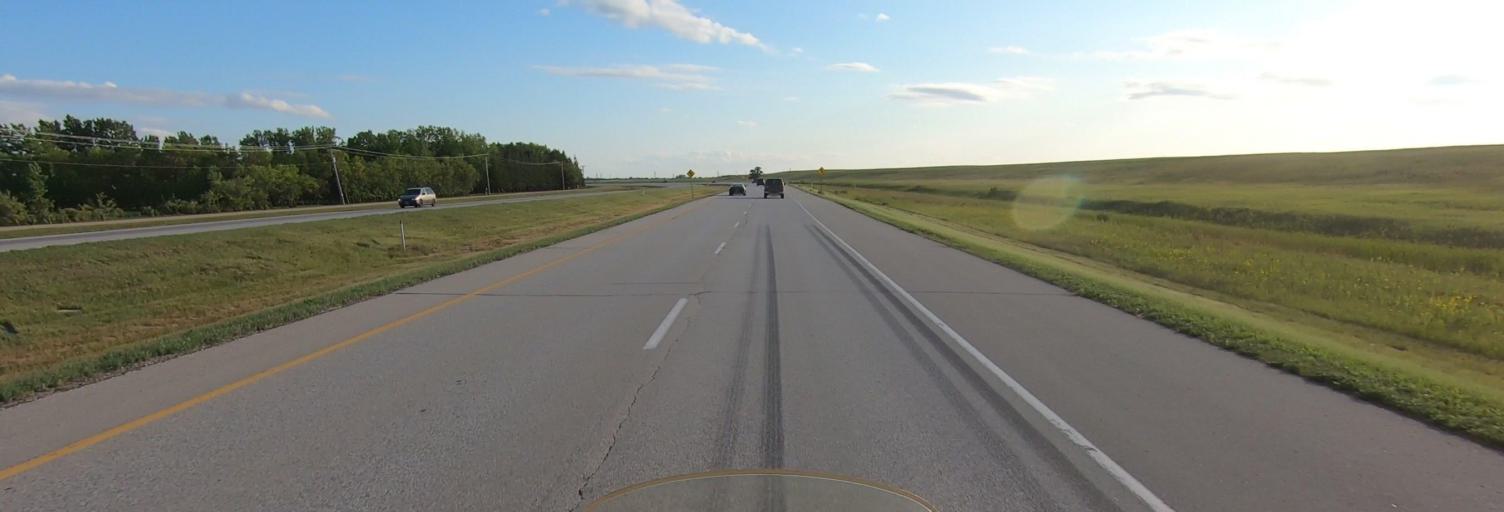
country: CA
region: Manitoba
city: Selkirk
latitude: 49.9955
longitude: -96.9729
